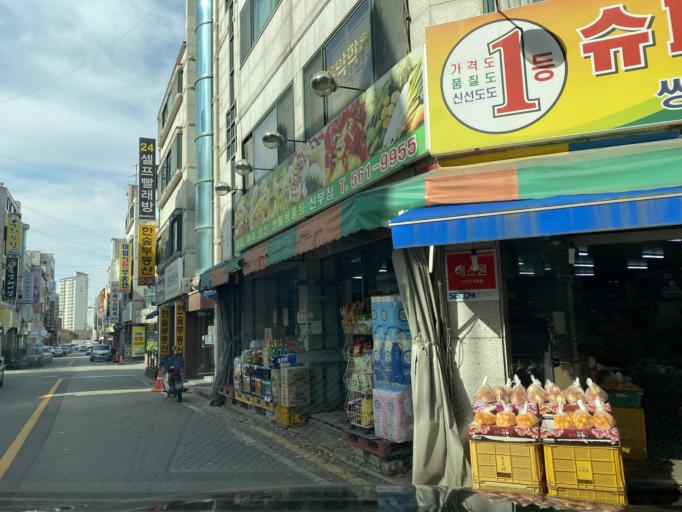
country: KR
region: Chungcheongnam-do
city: Cheonan
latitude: 36.8210
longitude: 127.1601
